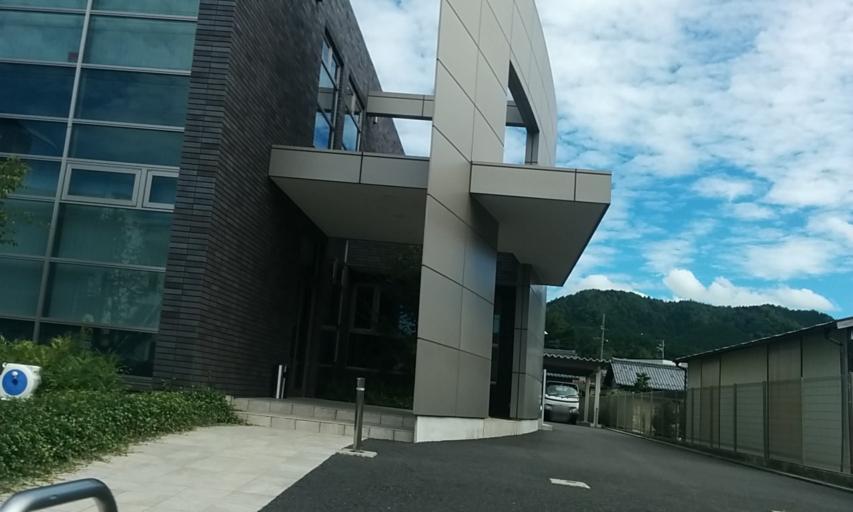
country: JP
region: Gifu
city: Minokamo
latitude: 35.5422
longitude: 137.1199
